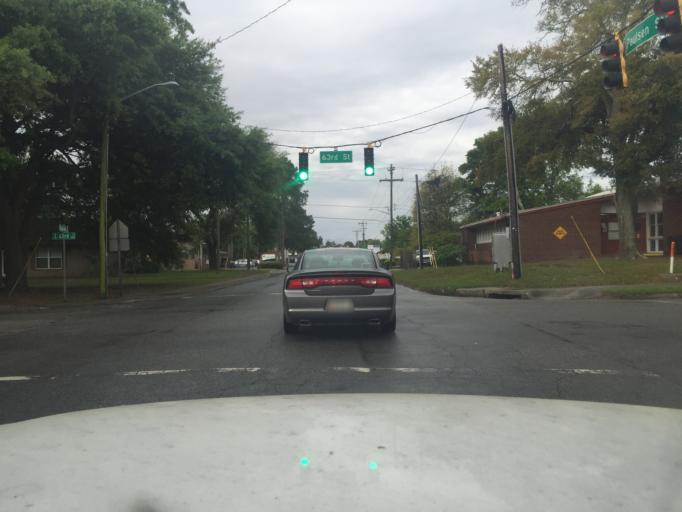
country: US
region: Georgia
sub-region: Chatham County
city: Thunderbolt
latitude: 32.0328
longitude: -81.0951
